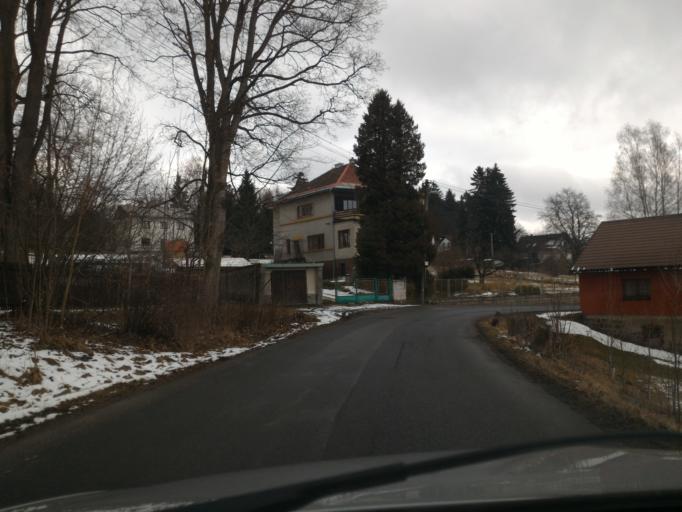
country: CZ
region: Liberecky
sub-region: Okres Jablonec nad Nisou
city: Smrzovka
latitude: 50.7326
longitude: 15.2430
